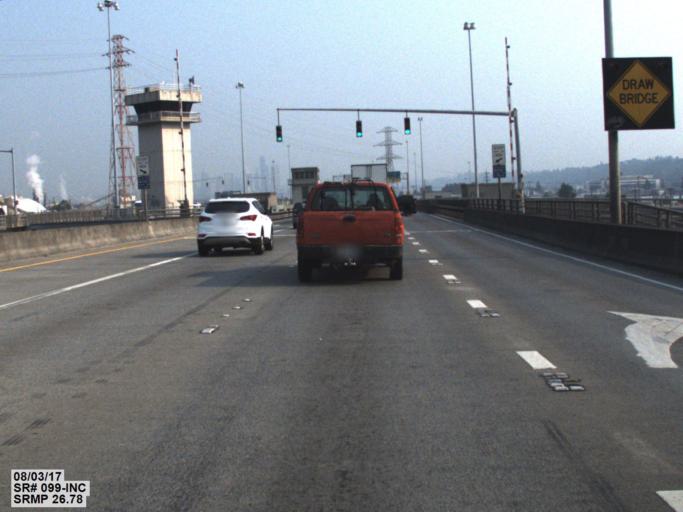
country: US
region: Washington
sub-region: King County
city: White Center
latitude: 47.5410
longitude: -122.3345
